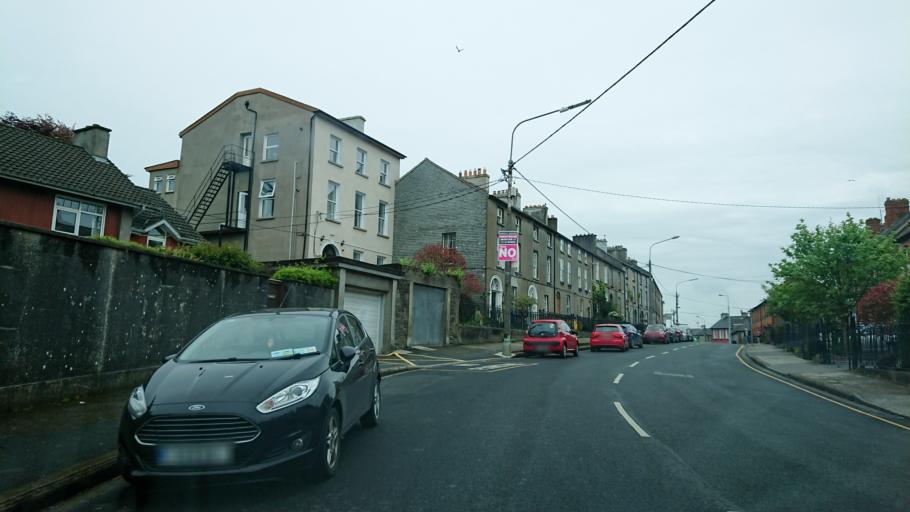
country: IE
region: Munster
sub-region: Waterford
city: Waterford
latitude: 52.2554
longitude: -7.1075
